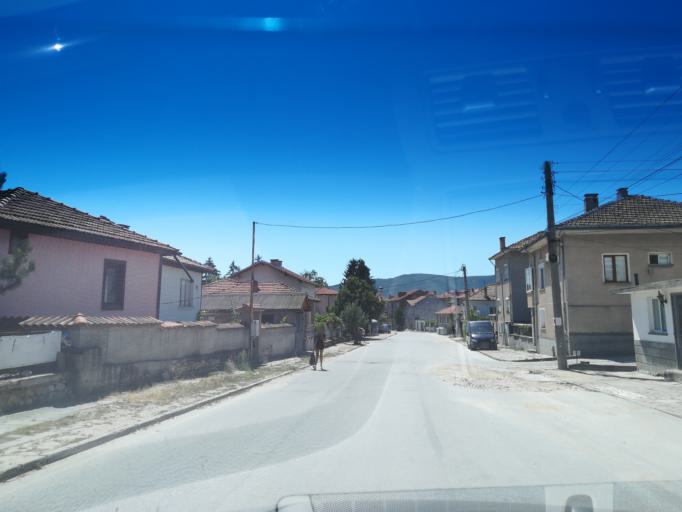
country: BG
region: Pazardzhik
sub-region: Obshtina Strelcha
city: Strelcha
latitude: 42.5120
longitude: 24.3206
